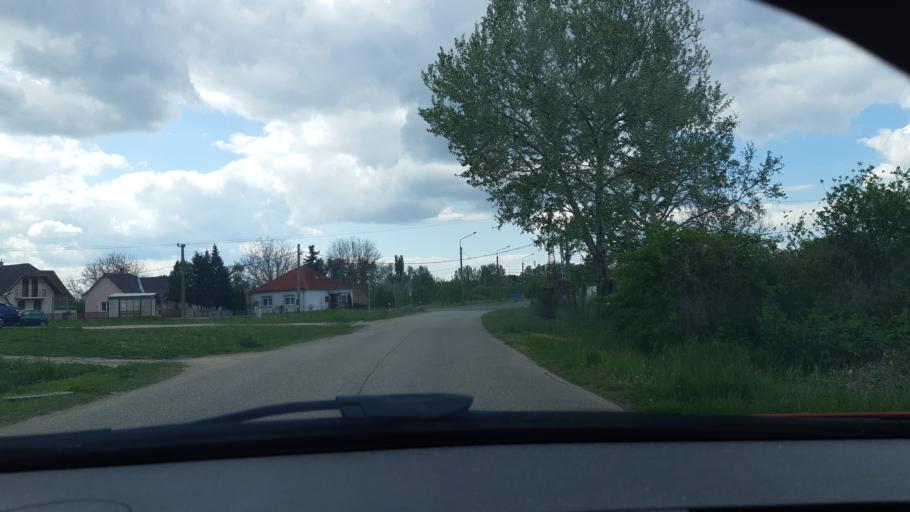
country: HU
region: Somogy
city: Kaposvar
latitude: 46.3633
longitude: 17.7623
